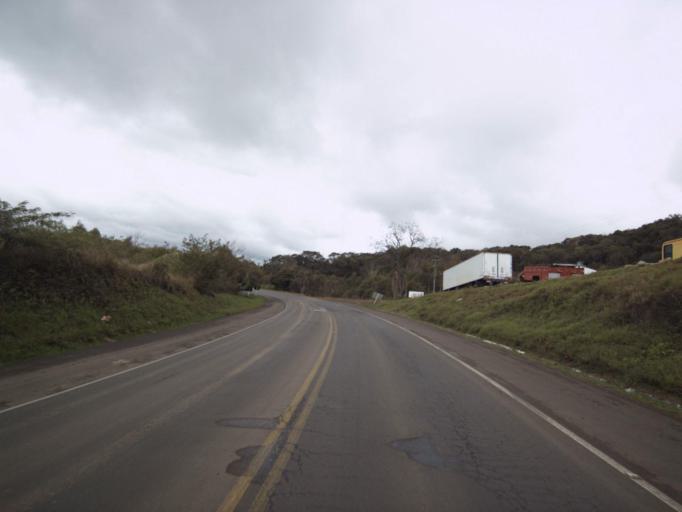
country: BR
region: Santa Catarina
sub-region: Concordia
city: Concordia
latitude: -27.2307
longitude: -51.9528
